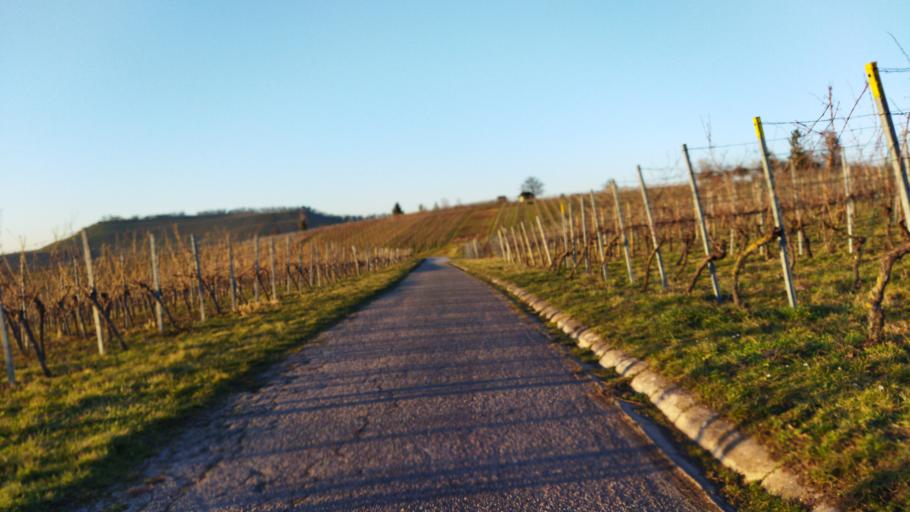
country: DE
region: Baden-Wuerttemberg
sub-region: Regierungsbezirk Stuttgart
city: Erlenbach
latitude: 49.1839
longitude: 9.2648
